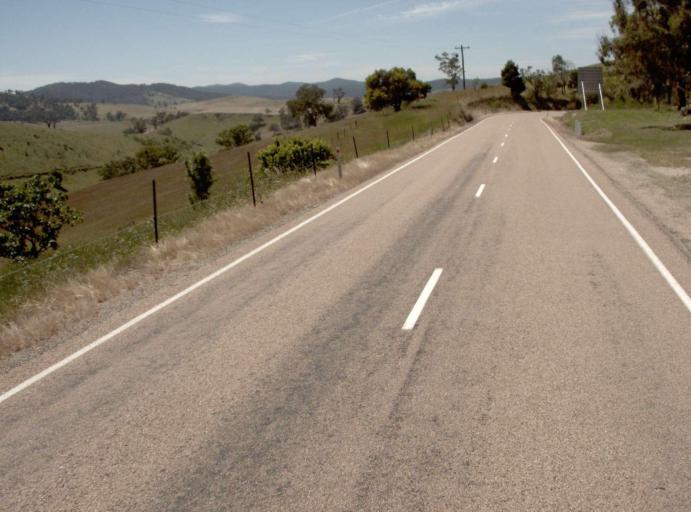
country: AU
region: Victoria
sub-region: East Gippsland
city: Lakes Entrance
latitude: -37.4827
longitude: 148.1856
